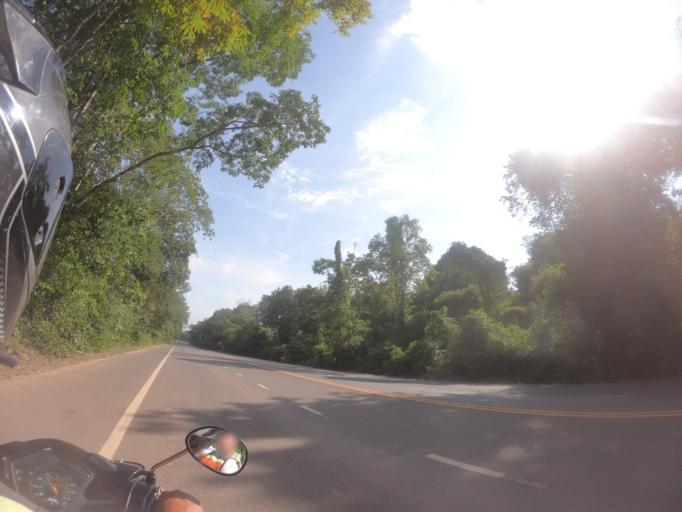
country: TH
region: Surin
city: Kap Choeng
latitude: 14.4435
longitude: 103.7007
